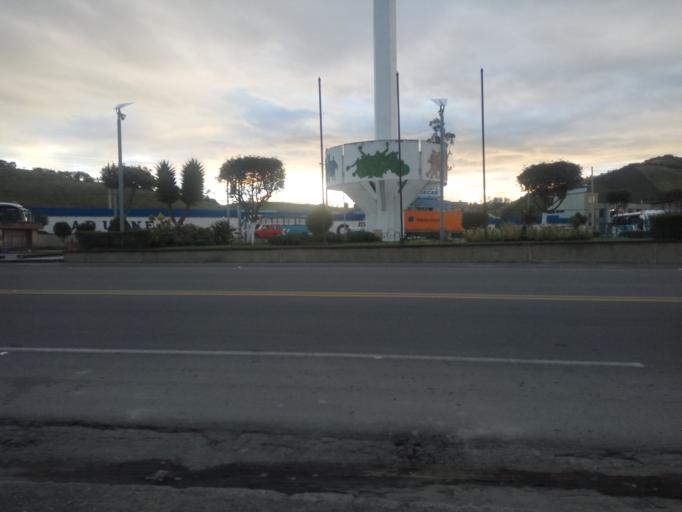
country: EC
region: Carchi
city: Tulcan
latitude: 0.7759
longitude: -77.7407
